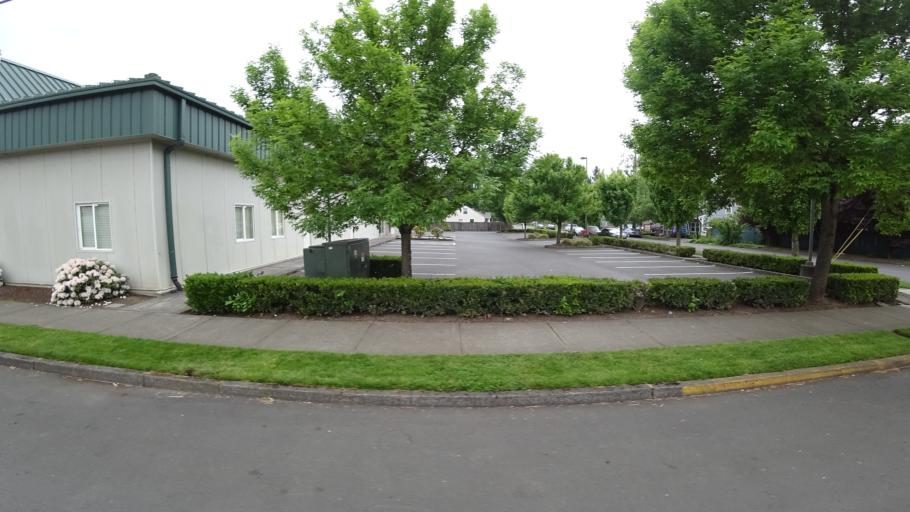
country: US
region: Oregon
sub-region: Washington County
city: Hillsboro
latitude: 45.5175
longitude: -122.9754
